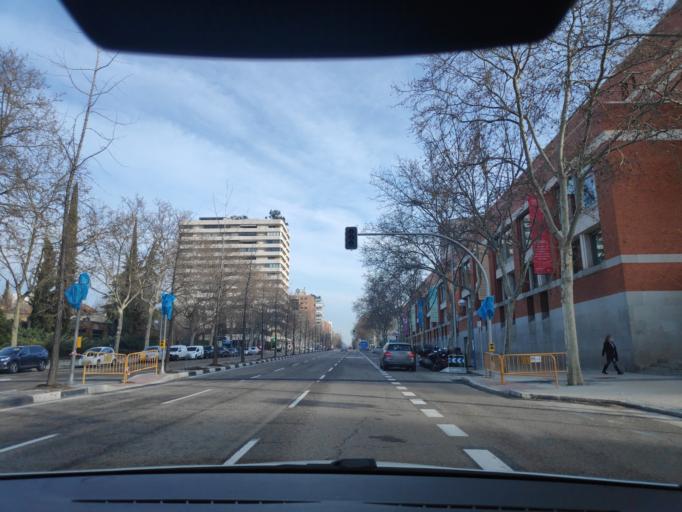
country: ES
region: Madrid
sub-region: Provincia de Madrid
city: Salamanca
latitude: 40.4454
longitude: -3.6783
